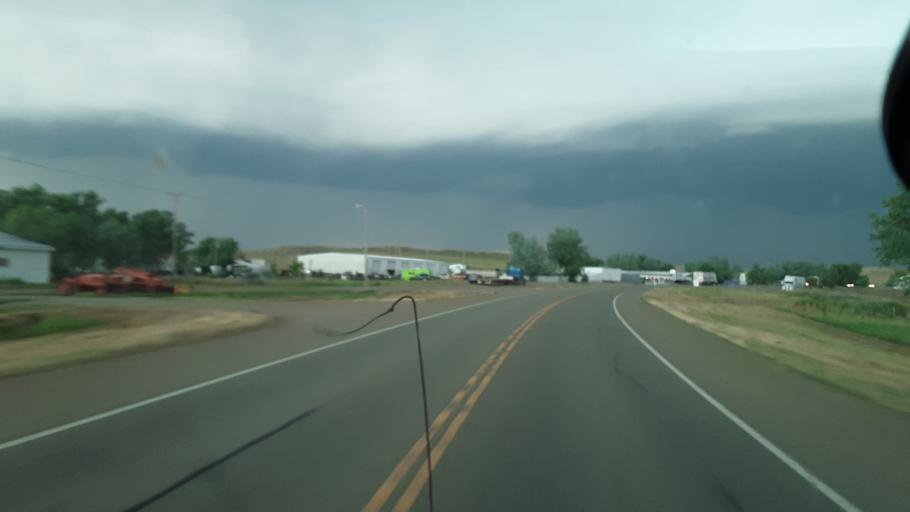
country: US
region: Montana
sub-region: Powder River County
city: Broadus
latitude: 45.4436
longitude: -105.4201
